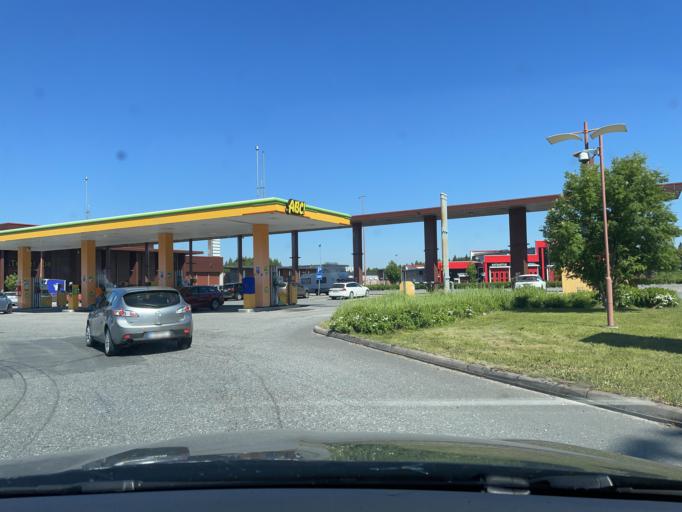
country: FI
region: Central Finland
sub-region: AEaenekoski
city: AEaenekoski
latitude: 62.5168
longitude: 25.6901
